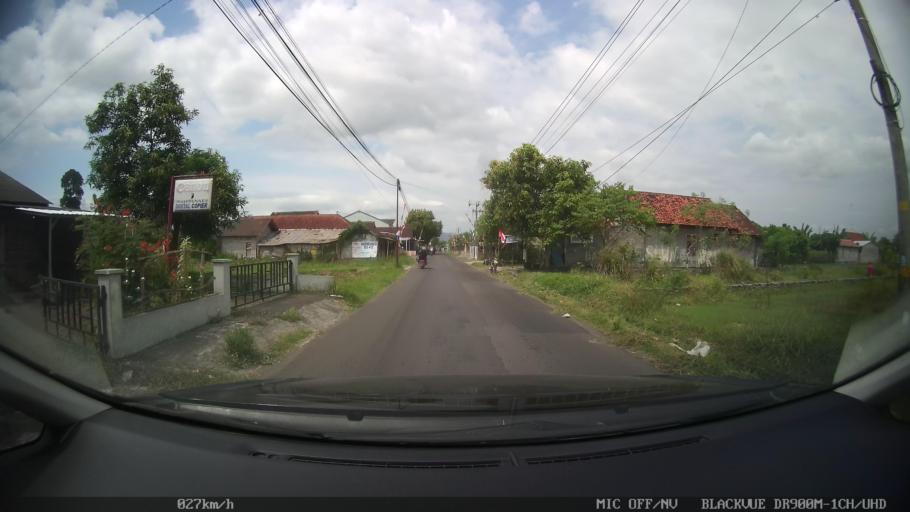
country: ID
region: Daerah Istimewa Yogyakarta
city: Depok
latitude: -7.7762
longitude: 110.4642
